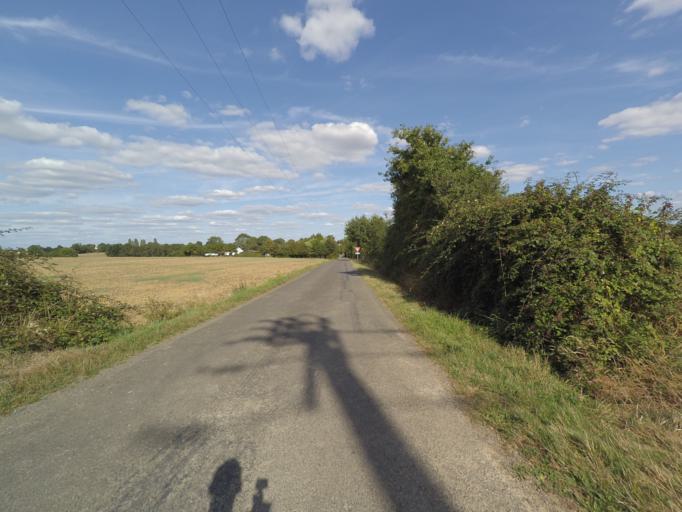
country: FR
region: Pays de la Loire
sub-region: Departement de la Loire-Atlantique
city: Vieillevigne
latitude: 46.9595
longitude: -1.4365
